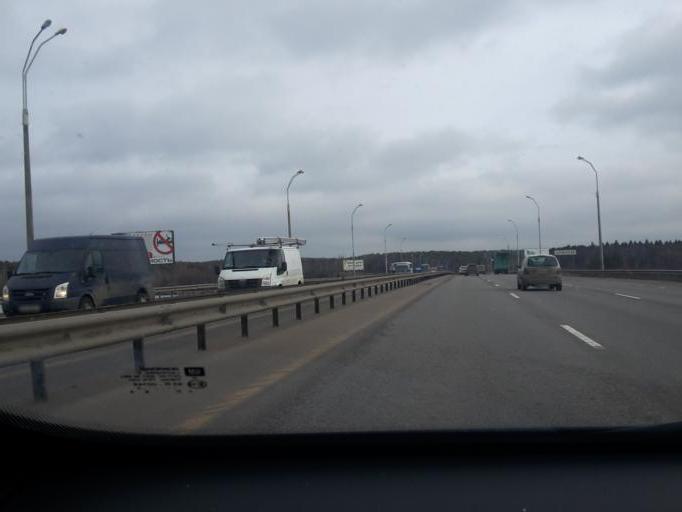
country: BY
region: Minsk
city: Zhdanovichy
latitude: 53.9569
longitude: 27.4535
